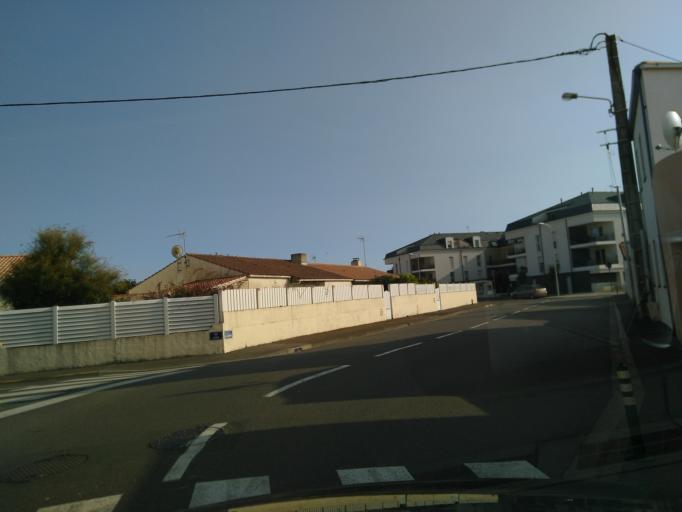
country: FR
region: Pays de la Loire
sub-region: Departement de la Vendee
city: Les Sables-d'Olonne
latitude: 46.4985
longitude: -1.8026
